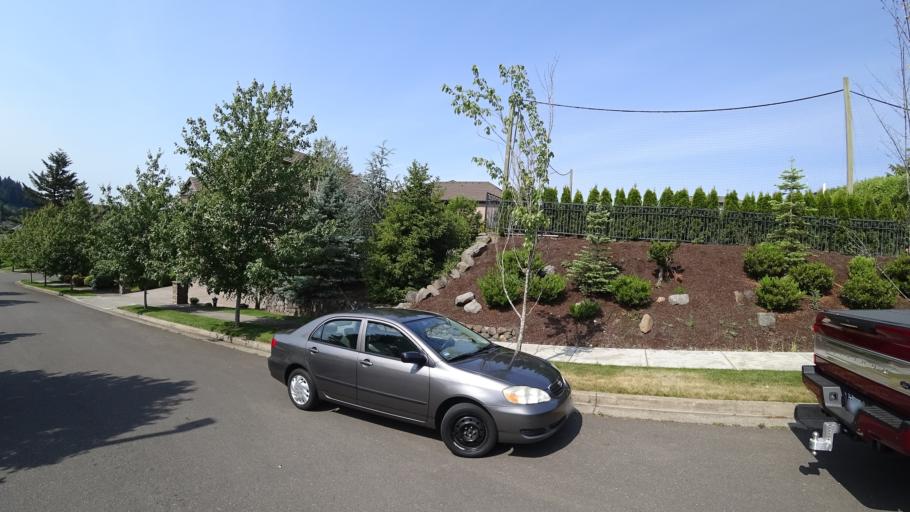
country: US
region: Oregon
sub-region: Clackamas County
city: Happy Valley
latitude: 45.4591
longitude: -122.5114
